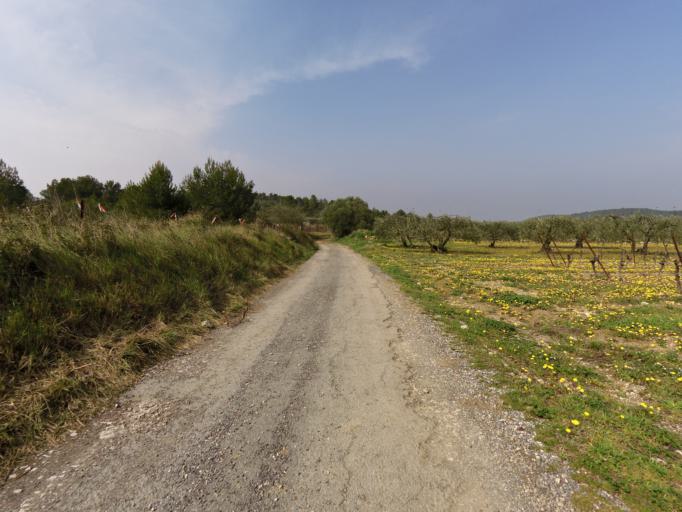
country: FR
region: Languedoc-Roussillon
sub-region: Departement du Gard
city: Congenies
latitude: 43.7651
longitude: 4.1662
